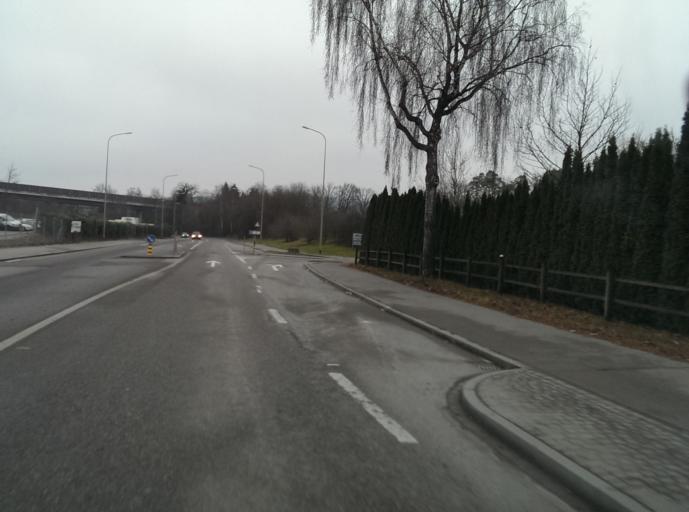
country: CH
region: Zurich
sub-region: Bezirk Dietikon
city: Dietikon / Hofacker
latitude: 47.4032
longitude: 8.4176
